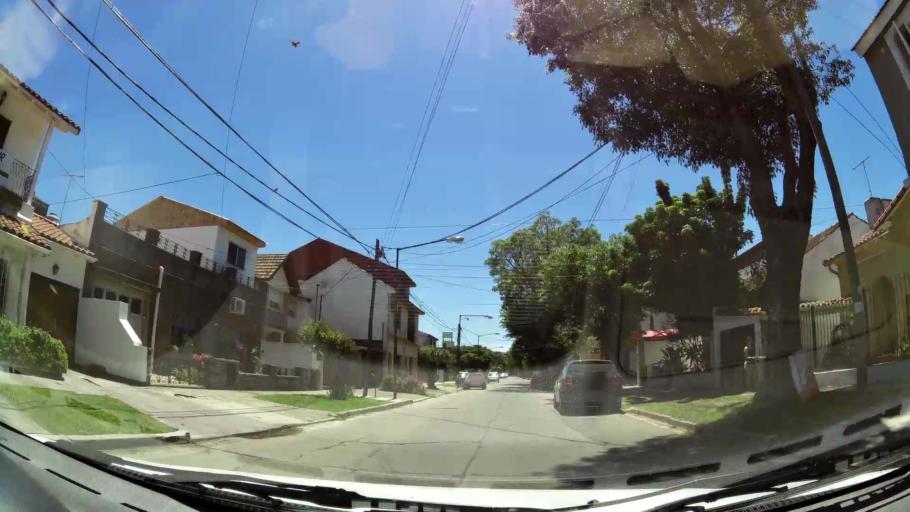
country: AR
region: Buenos Aires
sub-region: Partido de Vicente Lopez
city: Olivos
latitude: -34.5131
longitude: -58.5337
